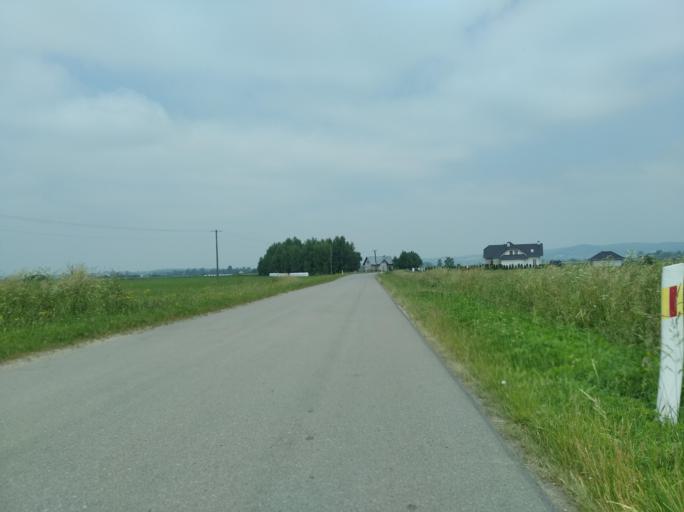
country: PL
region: Subcarpathian Voivodeship
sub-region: Powiat sanocki
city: Besko
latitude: 49.6048
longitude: 21.9566
